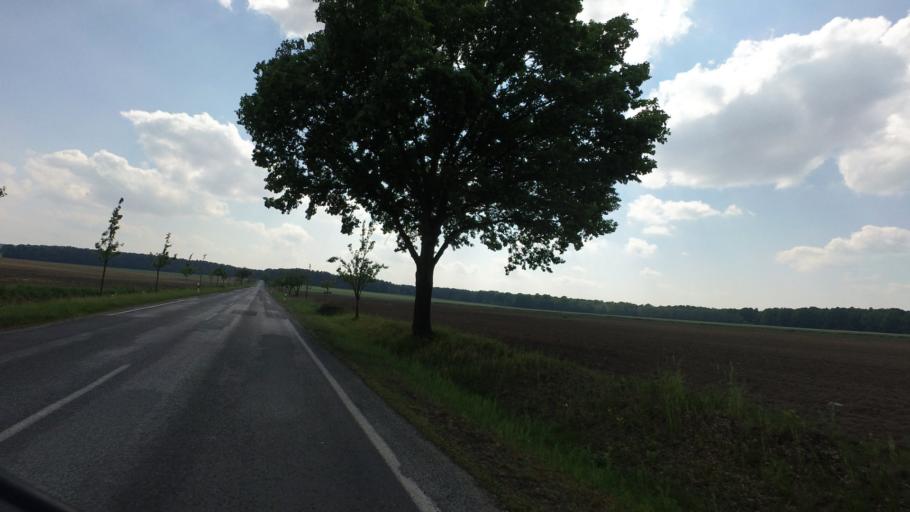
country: DE
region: Saxony
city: Mucka
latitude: 51.2941
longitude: 14.6613
